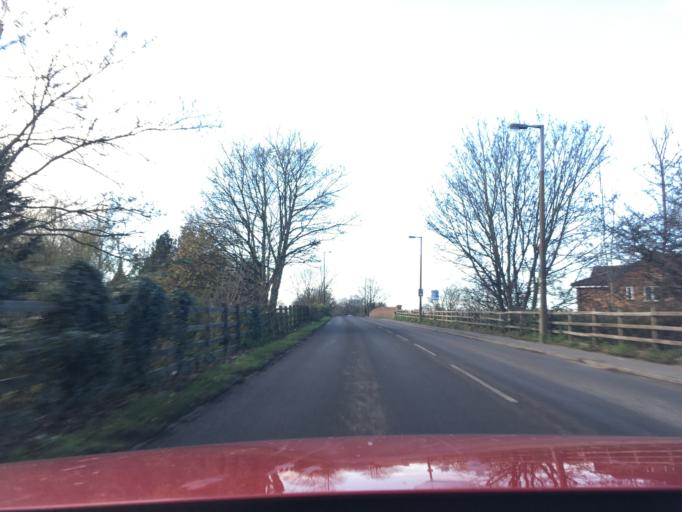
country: GB
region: England
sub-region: Staffordshire
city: Burton upon Trent
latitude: 52.7881
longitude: -1.6631
